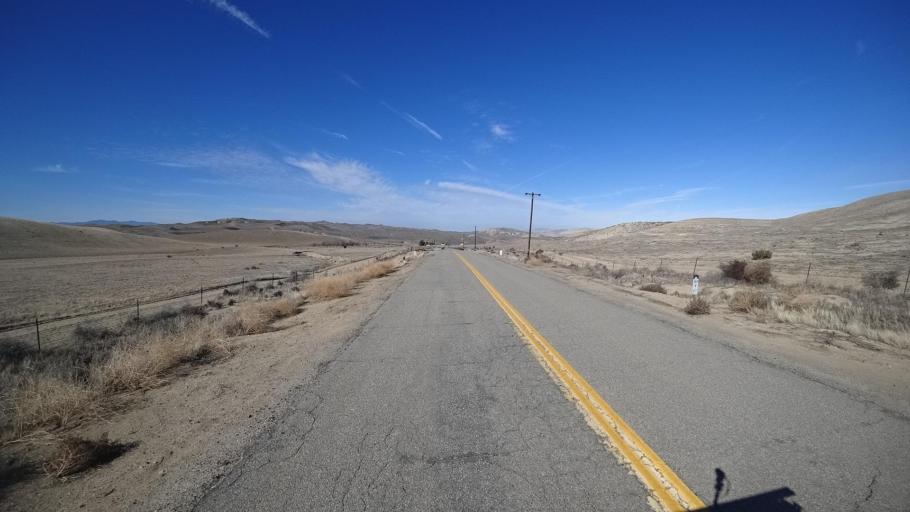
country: US
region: California
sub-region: Kern County
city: Maricopa
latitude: 34.9566
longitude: -119.4368
